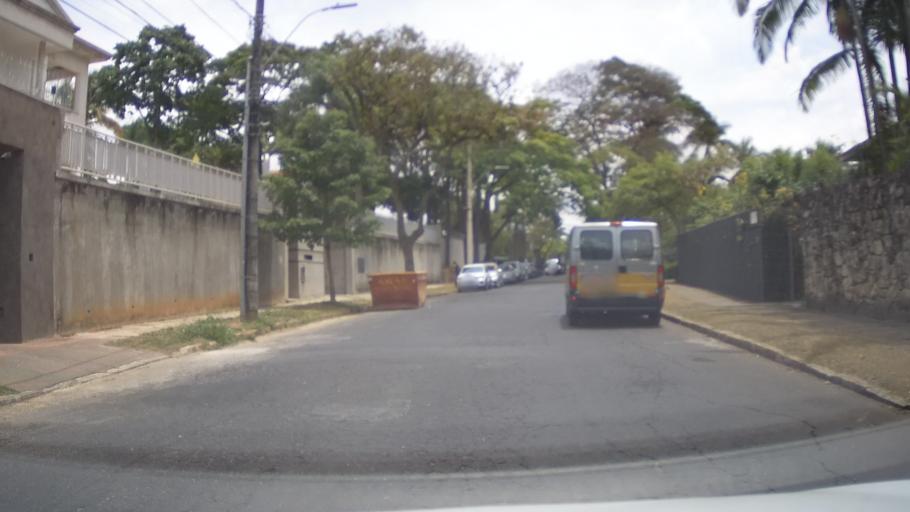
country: BR
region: Minas Gerais
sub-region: Belo Horizonte
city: Belo Horizonte
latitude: -19.8573
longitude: -43.9706
